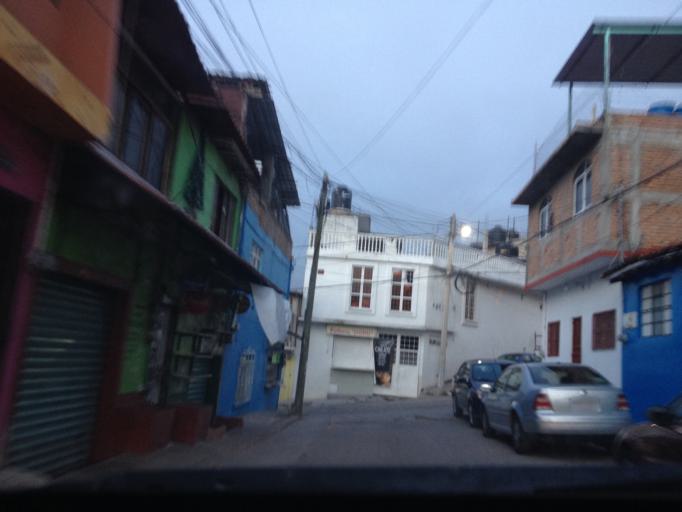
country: MX
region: Guerrero
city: Chilpancingo de los Bravos
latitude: 17.5602
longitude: -99.5018
